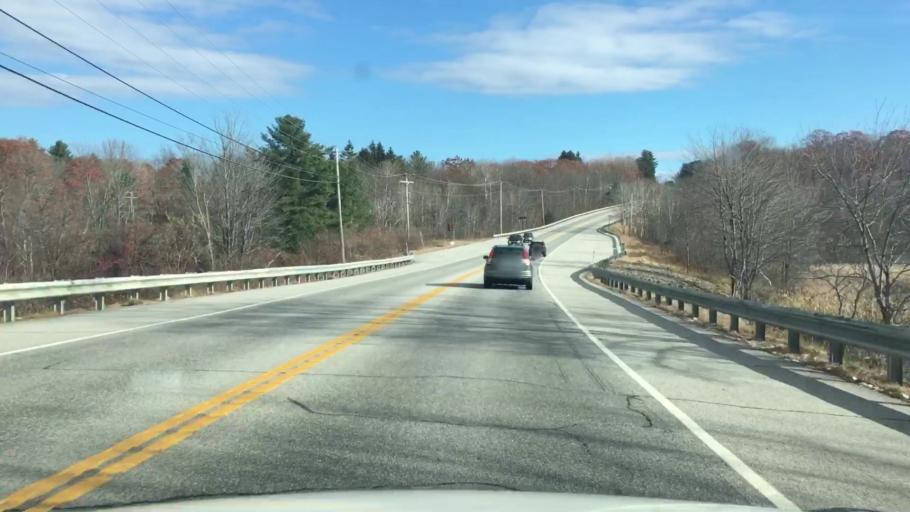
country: US
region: Maine
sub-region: Kennebec County
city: Winthrop
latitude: 44.3021
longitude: -69.9740
